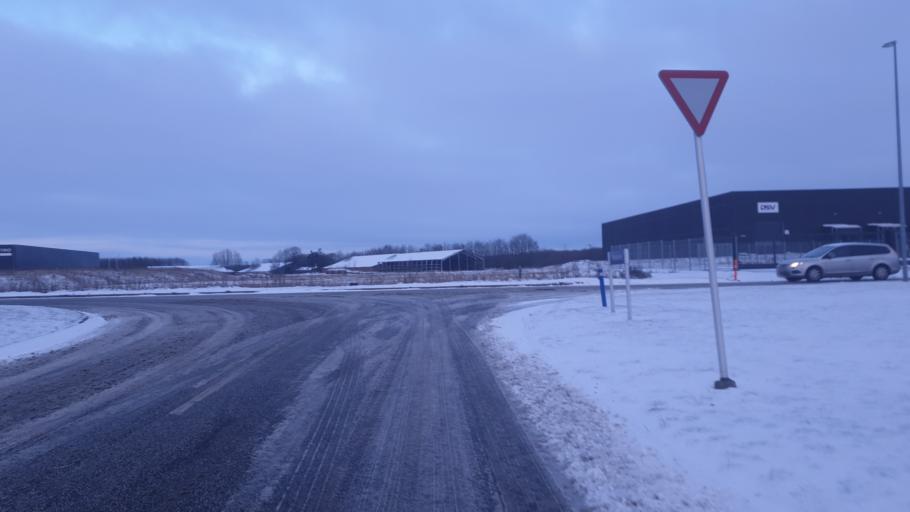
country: DK
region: Central Jutland
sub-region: Hedensted Kommune
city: Hedensted
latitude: 55.7894
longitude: 9.6796
